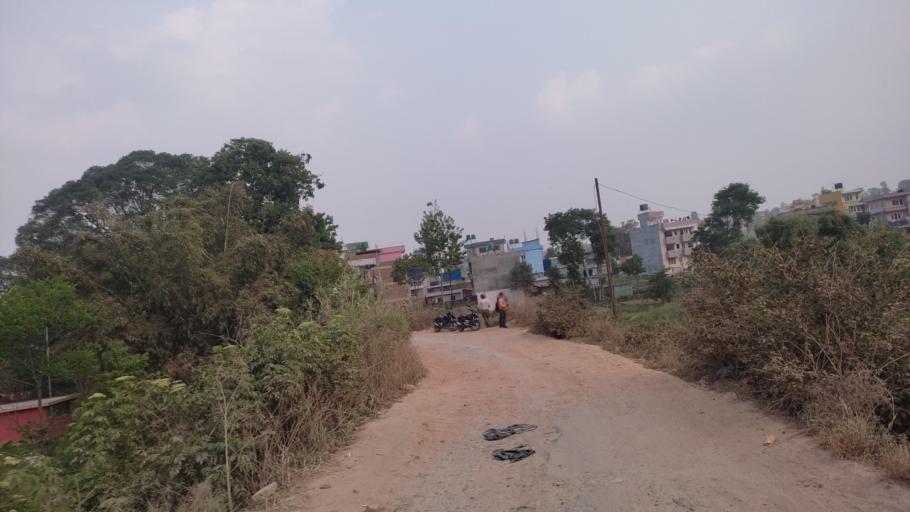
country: NP
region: Central Region
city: Kirtipur
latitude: 27.6820
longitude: 85.2601
